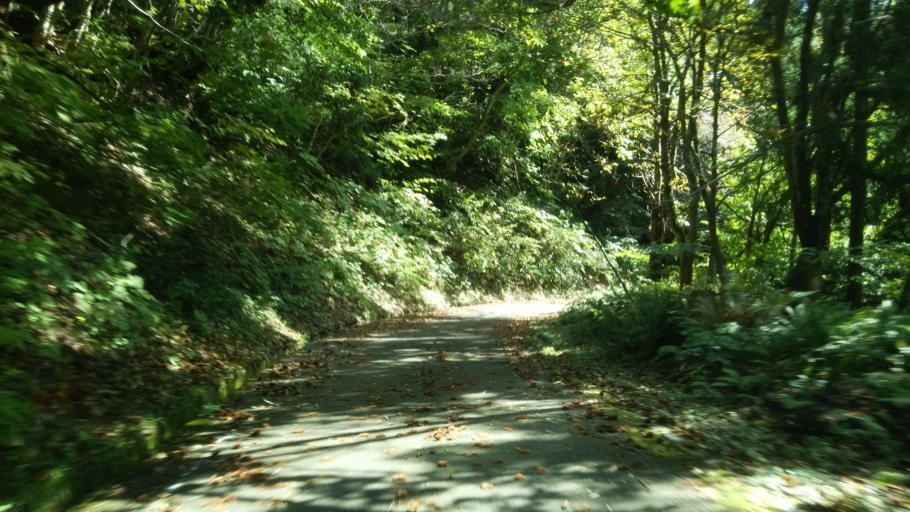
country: JP
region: Fukushima
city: Kitakata
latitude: 37.6133
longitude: 139.9784
